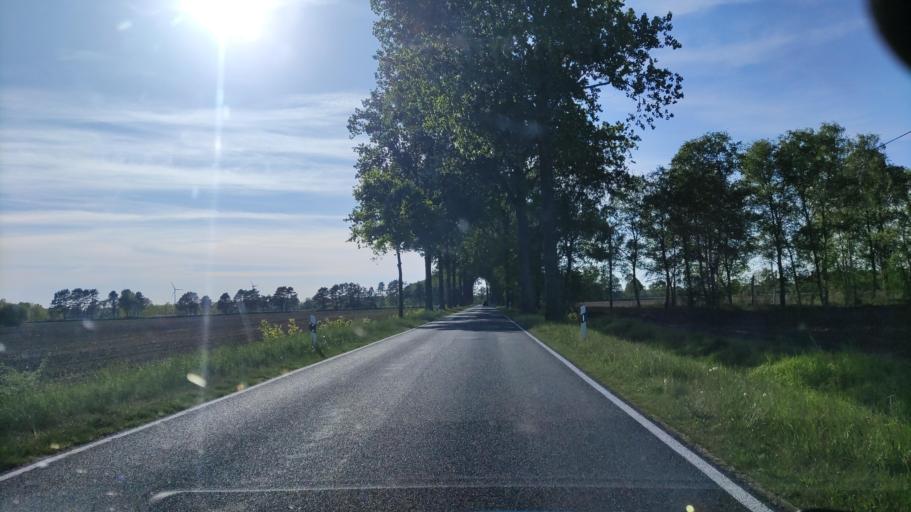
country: DE
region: Lower Saxony
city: Konigsmoor
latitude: 53.2228
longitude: 9.7010
